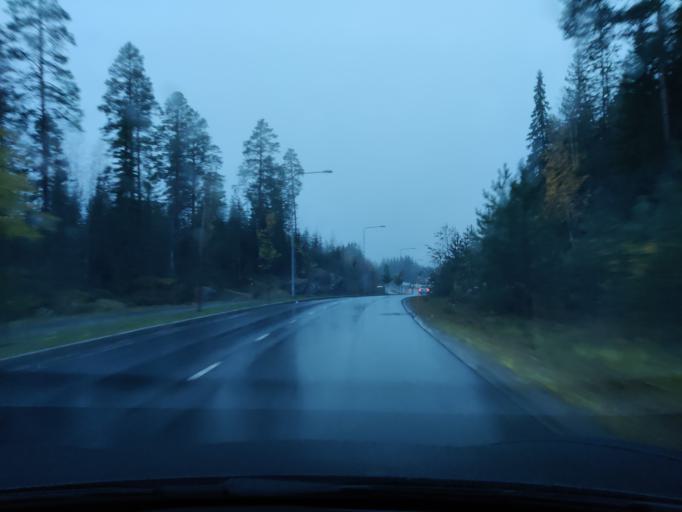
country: FI
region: Northern Savo
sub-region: Kuopio
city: Kuopio
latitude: 62.8318
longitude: 27.7103
